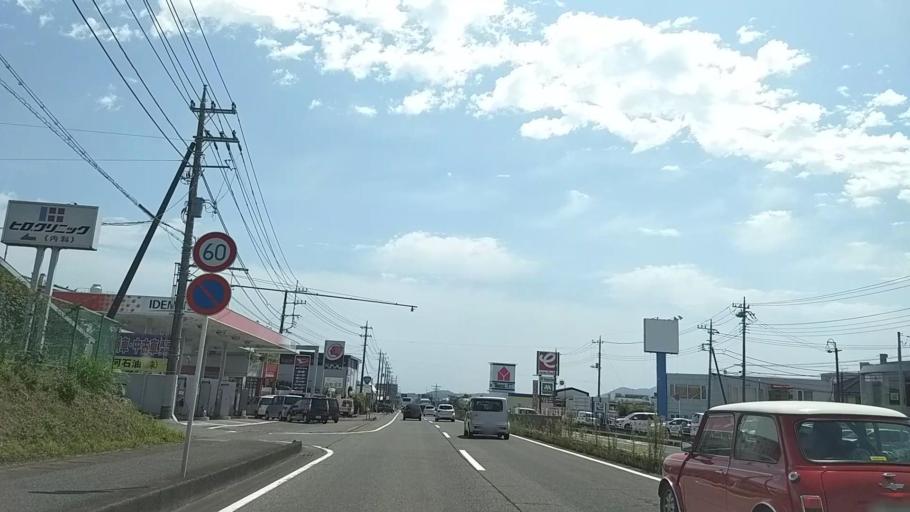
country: JP
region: Shizuoka
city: Fujinomiya
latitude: 35.2496
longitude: 138.6171
